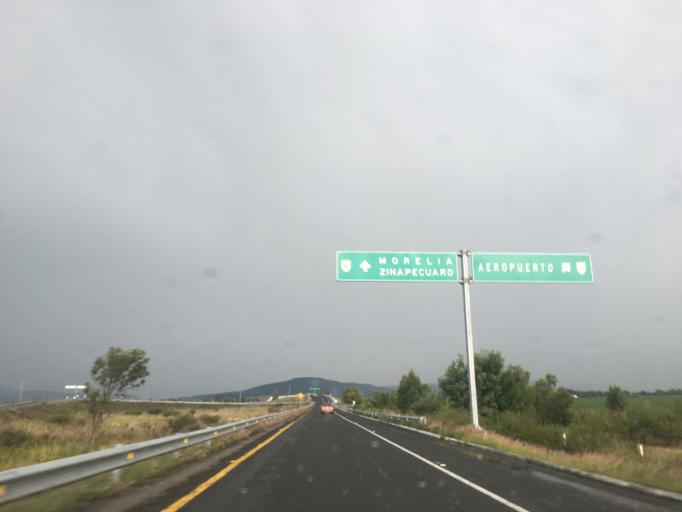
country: MX
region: Michoacan
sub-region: Alvaro Obregon
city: Lazaro Cardenas (La Purisima)
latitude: 19.8546
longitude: -101.0092
